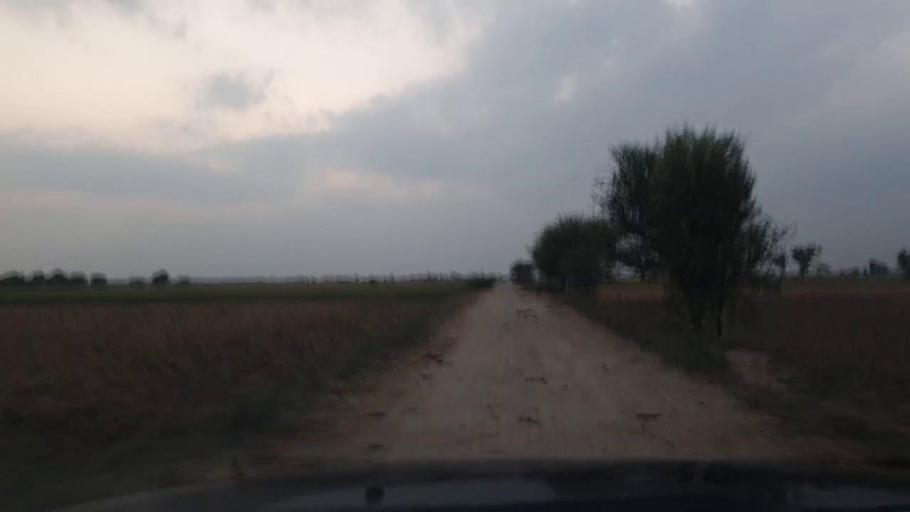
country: PK
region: Sindh
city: Jati
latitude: 24.5209
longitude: 68.3808
